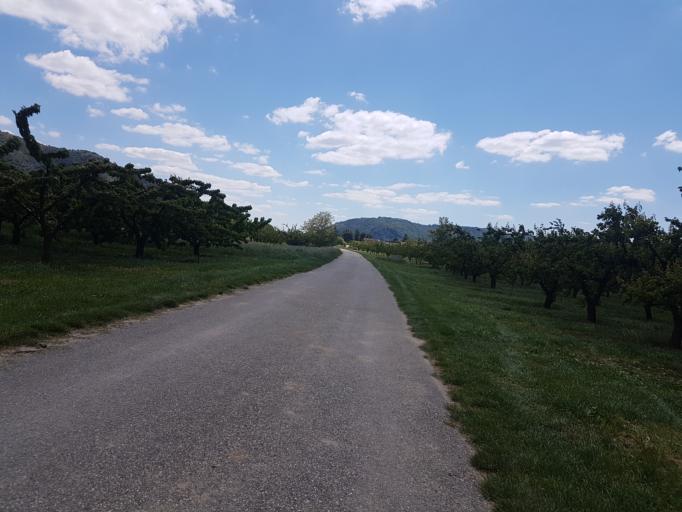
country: FR
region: Rhone-Alpes
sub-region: Departement de l'Ardeche
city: Saint-Jean-de-Muzols
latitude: 45.0982
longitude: 4.8222
